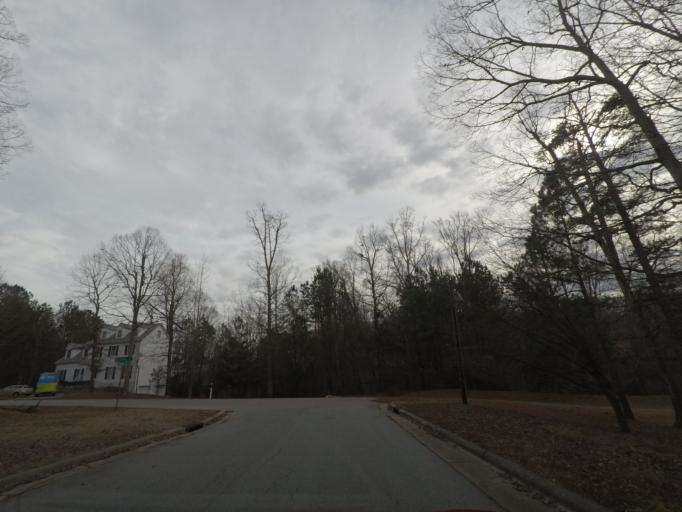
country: US
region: North Carolina
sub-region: Durham County
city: Durham
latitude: 36.0429
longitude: -78.9594
